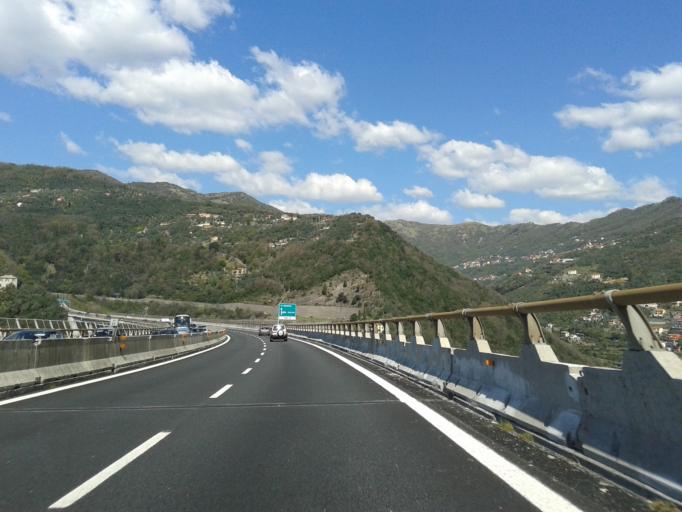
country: IT
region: Liguria
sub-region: Provincia di Genova
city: Avegno
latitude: 44.3721
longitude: 9.1530
